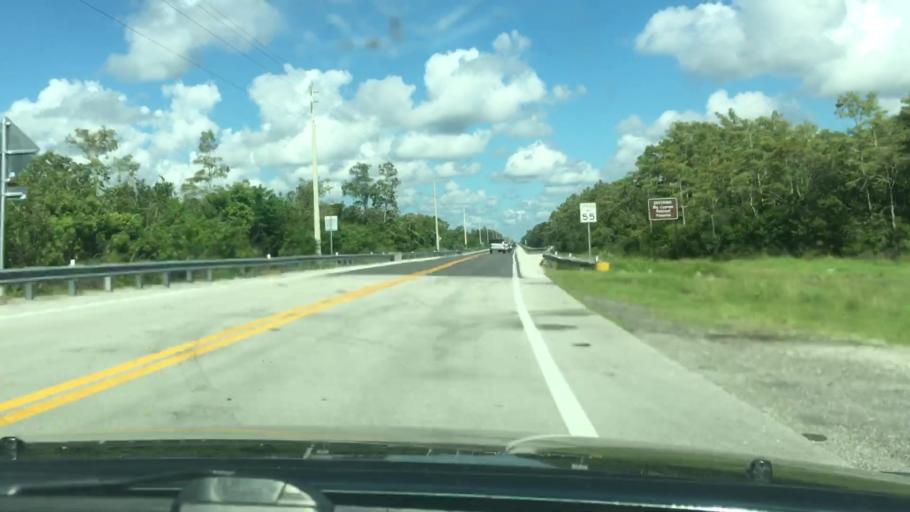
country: US
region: Florida
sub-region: Miami-Dade County
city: Kendall West
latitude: 25.7634
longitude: -80.8298
